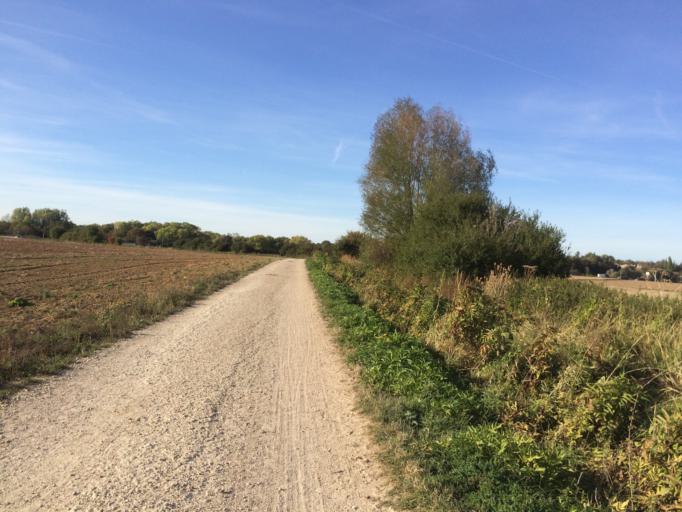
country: FR
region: Ile-de-France
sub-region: Departement de l'Essonne
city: Saclay
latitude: 48.7326
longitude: 2.1791
